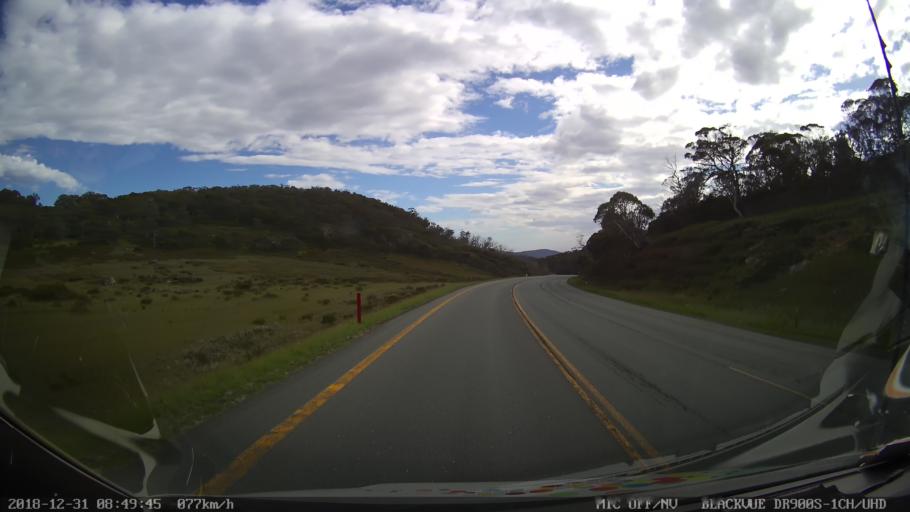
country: AU
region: New South Wales
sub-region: Snowy River
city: Jindabyne
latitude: -36.3589
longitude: 148.5102
